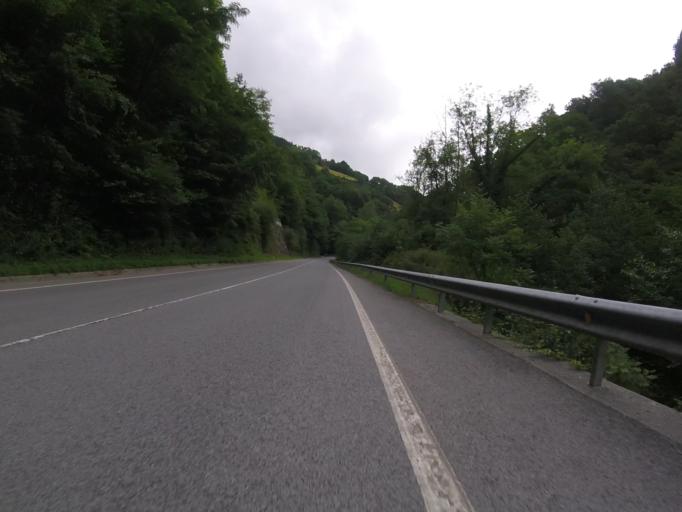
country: ES
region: Navarre
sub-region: Provincia de Navarra
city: Zubieta
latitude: 43.1157
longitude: -1.7583
